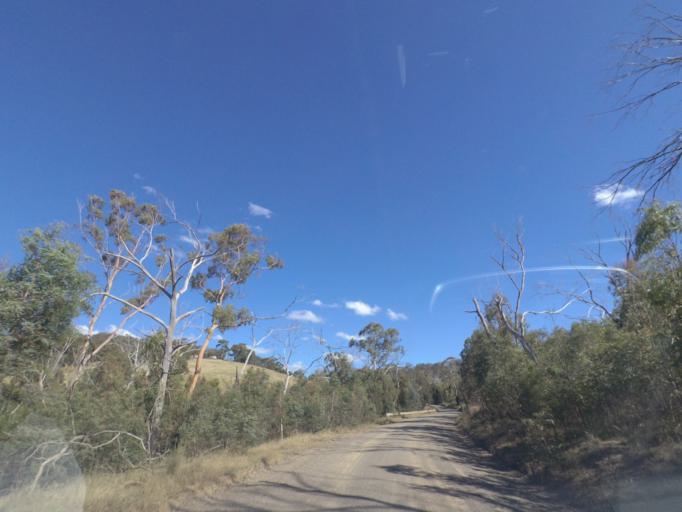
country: AU
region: Victoria
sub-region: Hume
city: Craigieburn
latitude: -37.4278
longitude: 144.9282
